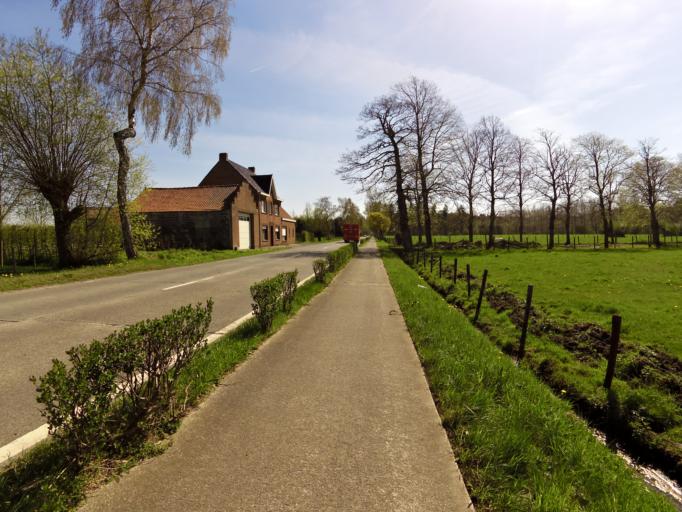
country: BE
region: Flanders
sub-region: Provincie West-Vlaanderen
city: Jabbeke
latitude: 51.1618
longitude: 3.0850
